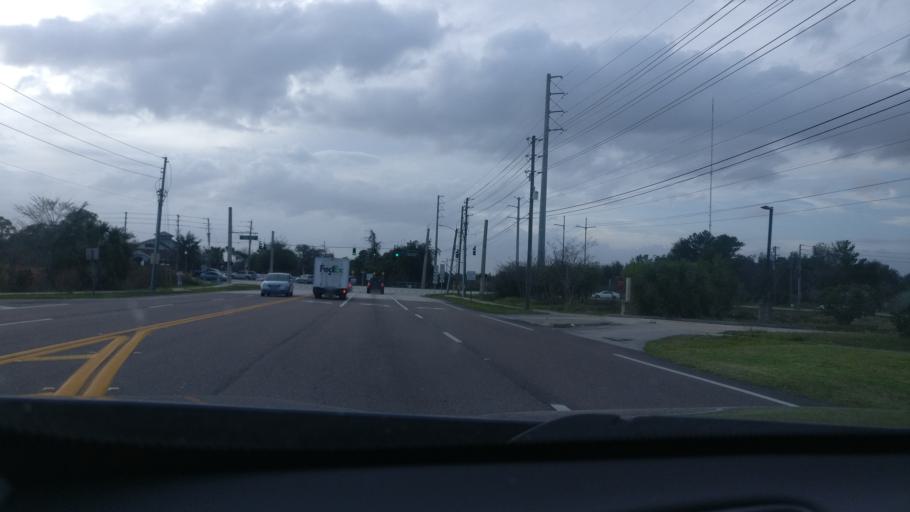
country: US
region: Florida
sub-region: Volusia County
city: DeBary
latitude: 28.9120
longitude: -81.3014
